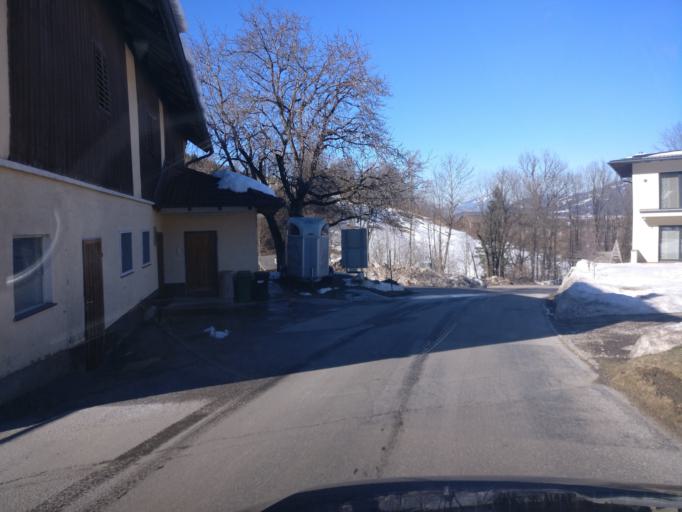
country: AT
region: Salzburg
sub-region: Politischer Bezirk Hallein
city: Kuchl
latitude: 47.6106
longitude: 13.1405
